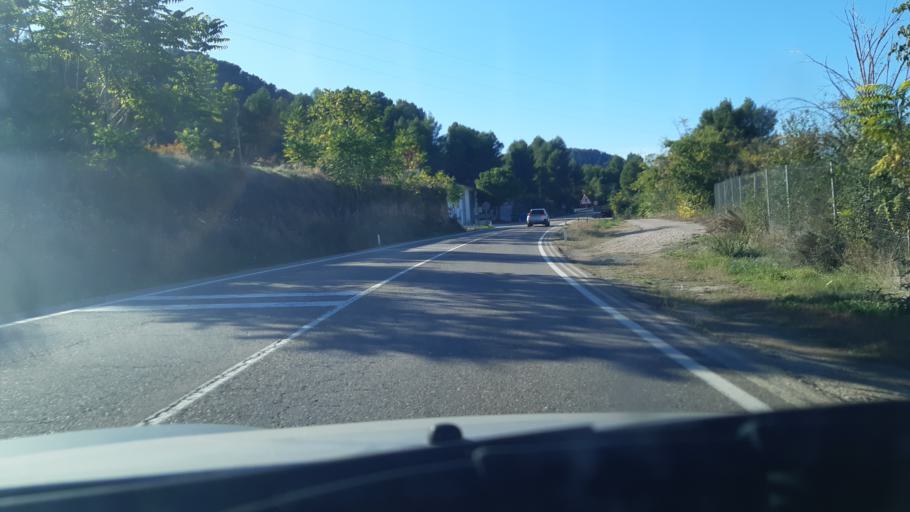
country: ES
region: Aragon
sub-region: Provincia de Teruel
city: Valderrobres
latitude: 40.8723
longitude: 0.1460
